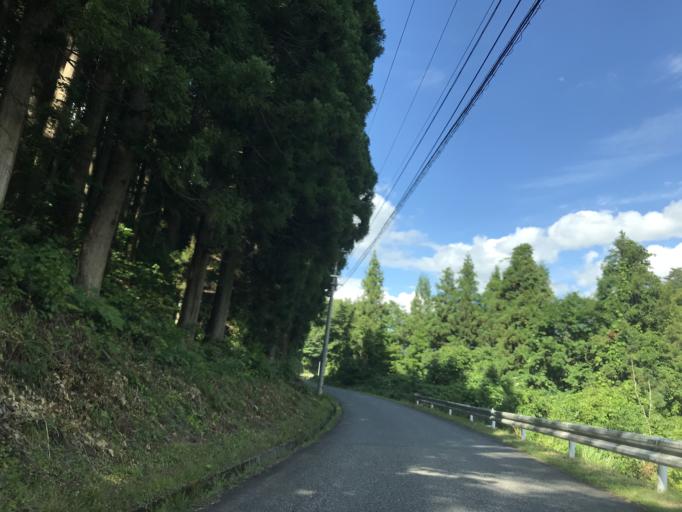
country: JP
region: Iwate
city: Ichinoseki
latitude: 38.9348
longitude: 140.9830
